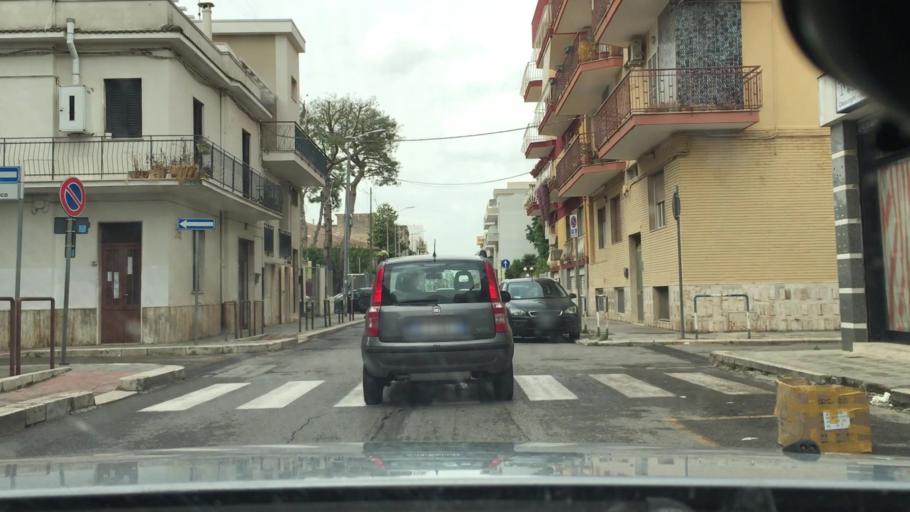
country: IT
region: Apulia
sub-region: Provincia di Bari
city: Capurso
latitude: 41.0480
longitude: 16.9255
